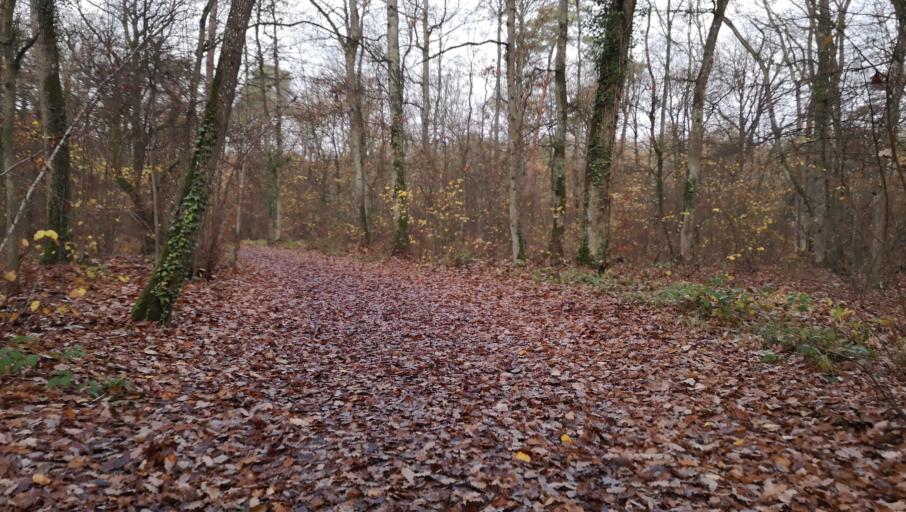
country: FR
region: Centre
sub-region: Departement du Loiret
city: Semoy
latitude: 47.9420
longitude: 1.9661
